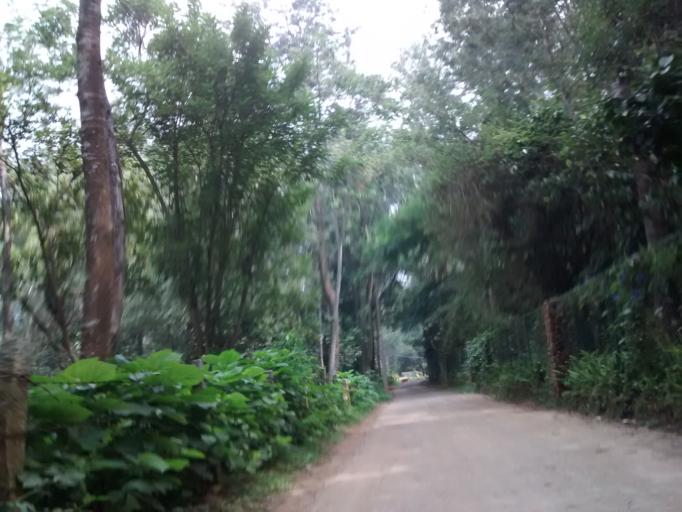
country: IN
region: Tamil Nadu
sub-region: Salem
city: Salem
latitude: 11.7911
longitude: 78.2016
